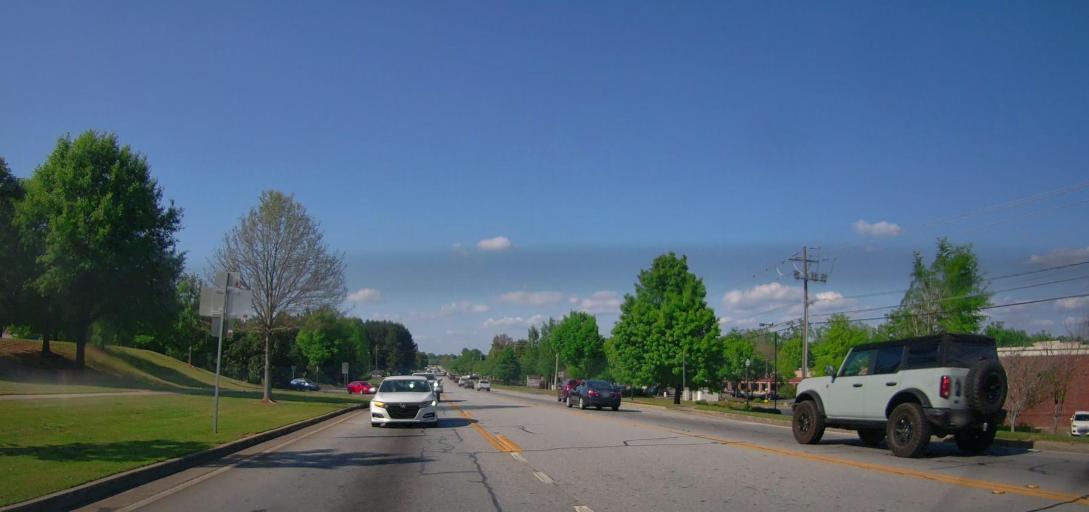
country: US
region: Georgia
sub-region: Morgan County
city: Madison
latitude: 33.5653
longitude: -83.4783
